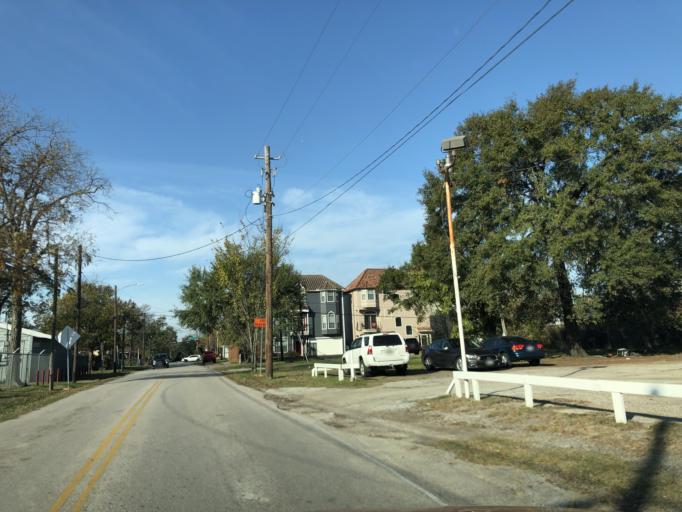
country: US
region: Texas
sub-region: Harris County
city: Houston
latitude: 29.7961
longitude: -95.4101
